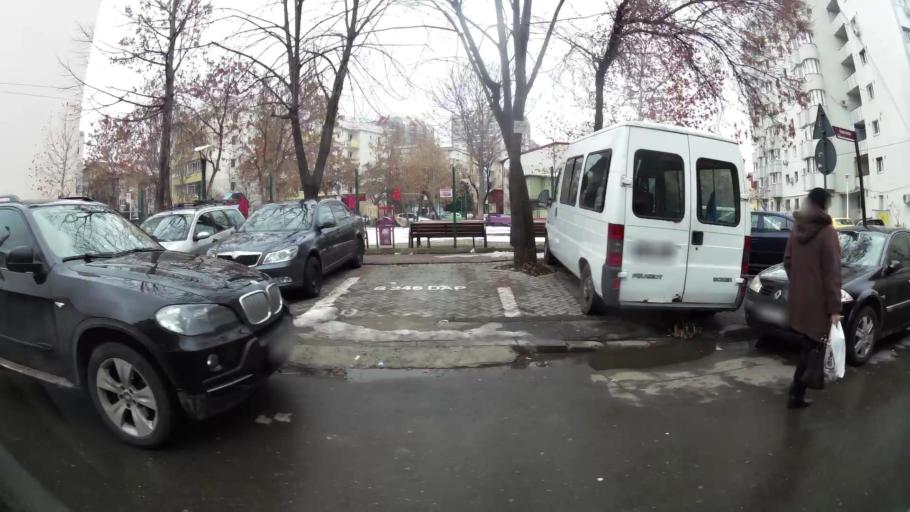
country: RO
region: Bucuresti
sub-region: Municipiul Bucuresti
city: Bucharest
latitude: 44.4174
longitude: 26.1332
